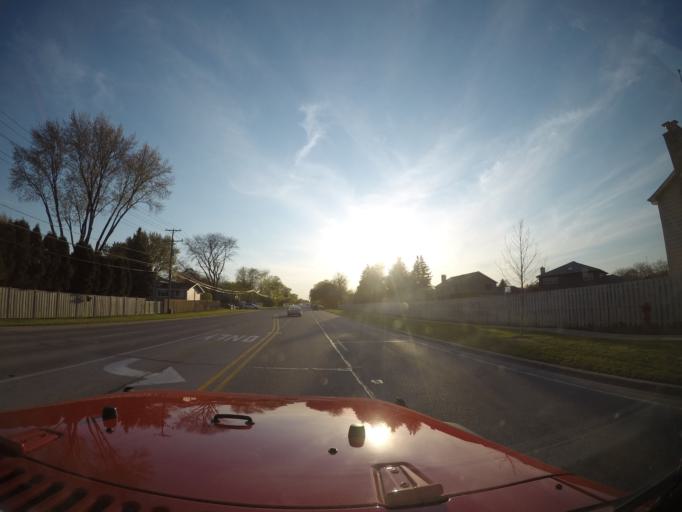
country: US
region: Illinois
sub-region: Cook County
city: Prospect Heights
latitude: 42.0878
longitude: -87.9159
